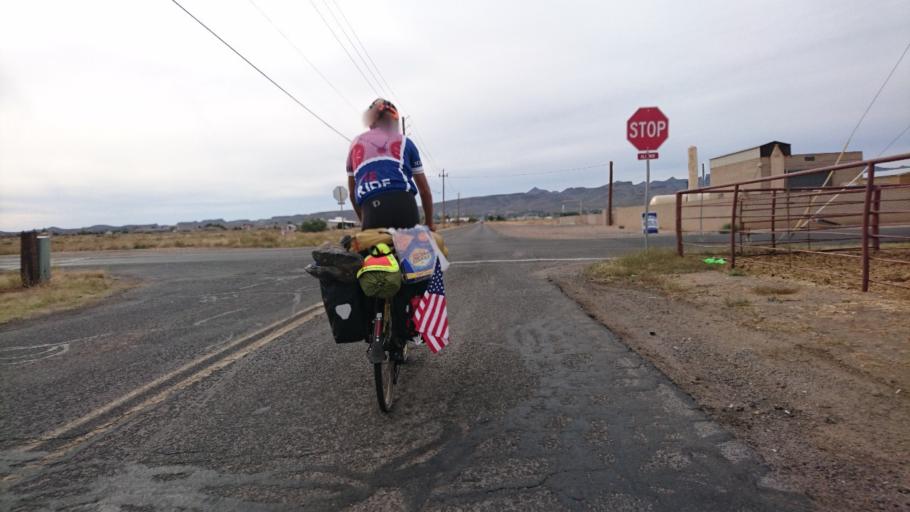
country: US
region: Arizona
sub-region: Mohave County
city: New Kingman-Butler
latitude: 35.2394
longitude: -113.9935
